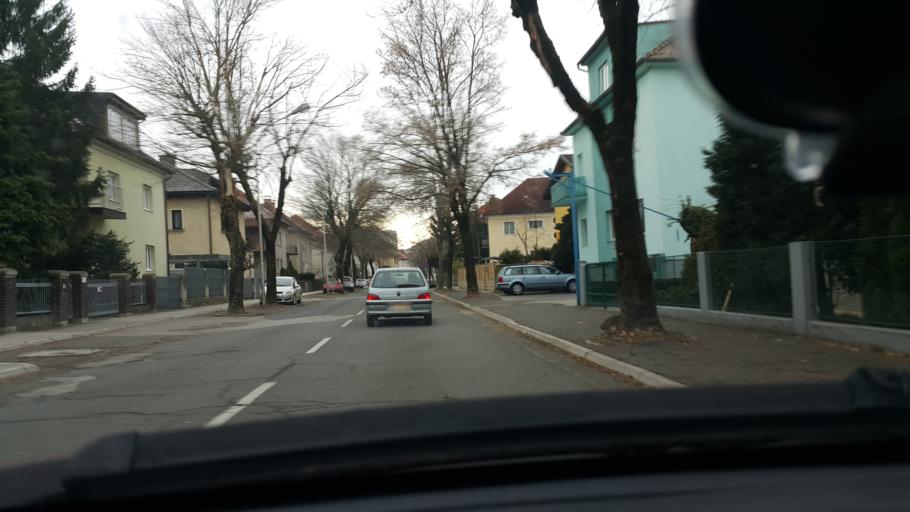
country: SI
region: Maribor
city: Maribor
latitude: 46.5446
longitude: 15.6431
